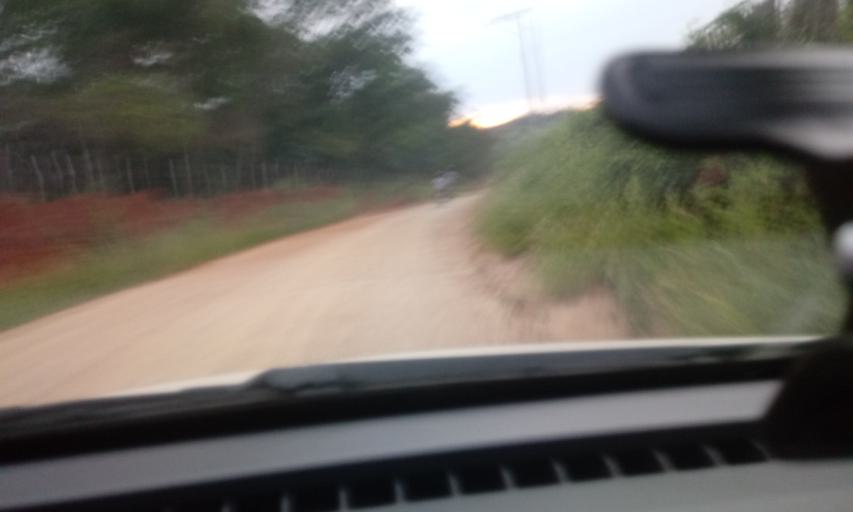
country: BR
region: Bahia
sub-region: Riacho De Santana
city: Riacho de Santana
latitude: -13.8138
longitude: -42.7607
